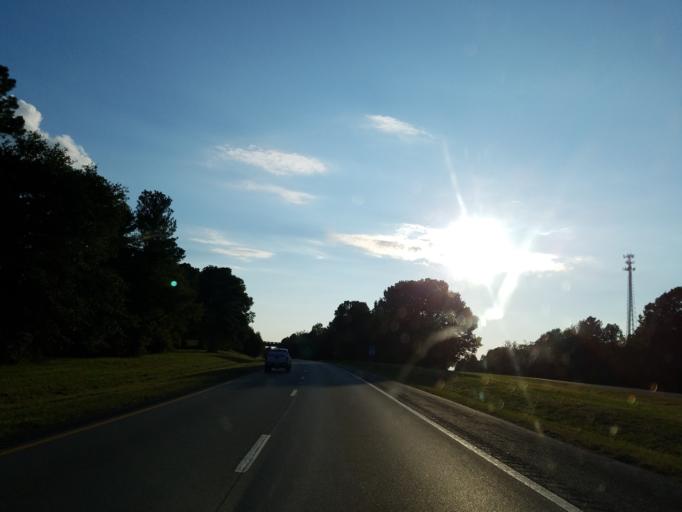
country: US
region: North Carolina
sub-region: Cleveland County
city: White Plains
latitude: 35.1960
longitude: -81.3910
